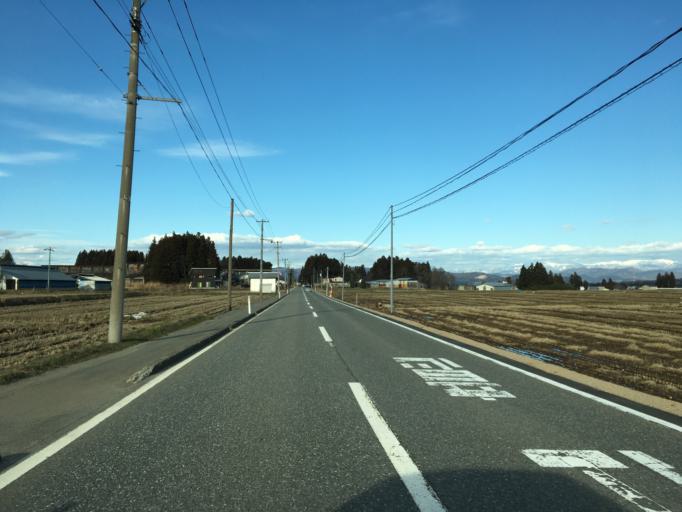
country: JP
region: Yamagata
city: Nagai
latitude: 38.0336
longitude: 139.9835
